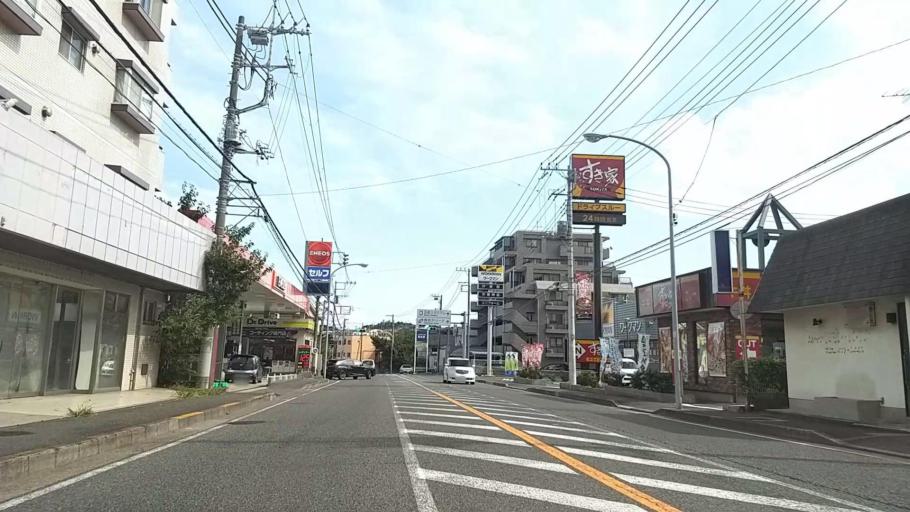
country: JP
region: Kanagawa
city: Yokohama
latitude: 35.5098
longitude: 139.5863
